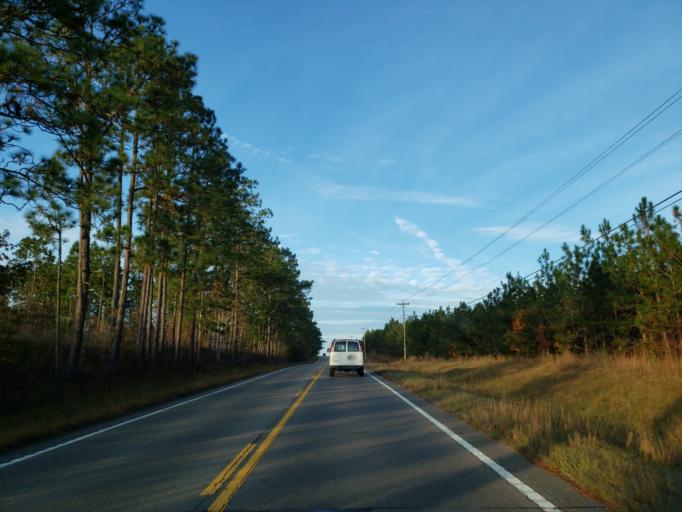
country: US
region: Mississippi
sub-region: Lamar County
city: West Hattiesburg
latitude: 31.2323
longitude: -89.3514
